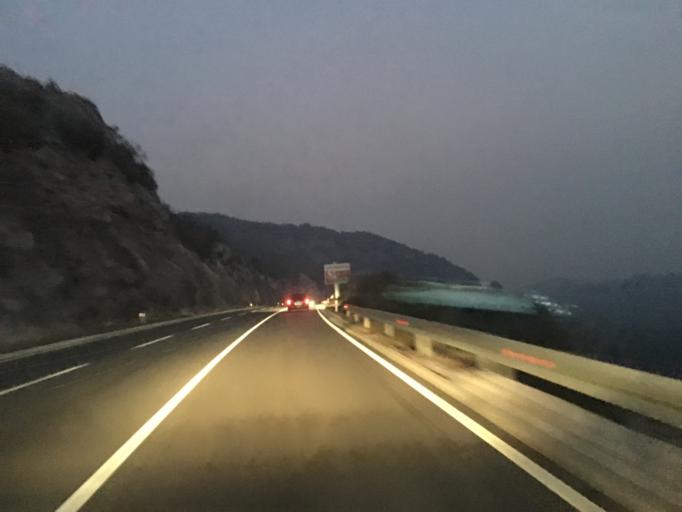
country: ME
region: Cetinje
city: Cetinje
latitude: 42.3795
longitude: 19.0245
